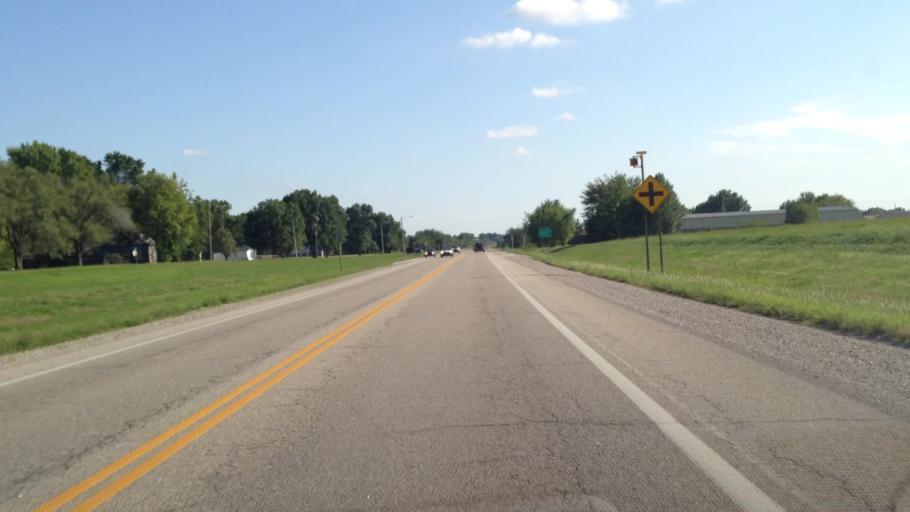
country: US
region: Kansas
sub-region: Crawford County
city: Arma
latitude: 37.5454
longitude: -94.7102
